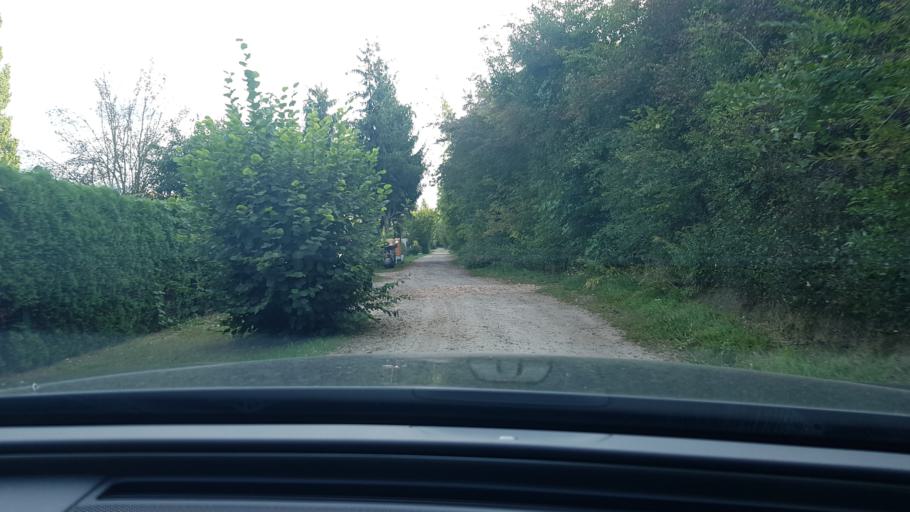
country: DE
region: Brandenburg
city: Brieselang
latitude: 52.5959
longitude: 12.9813
